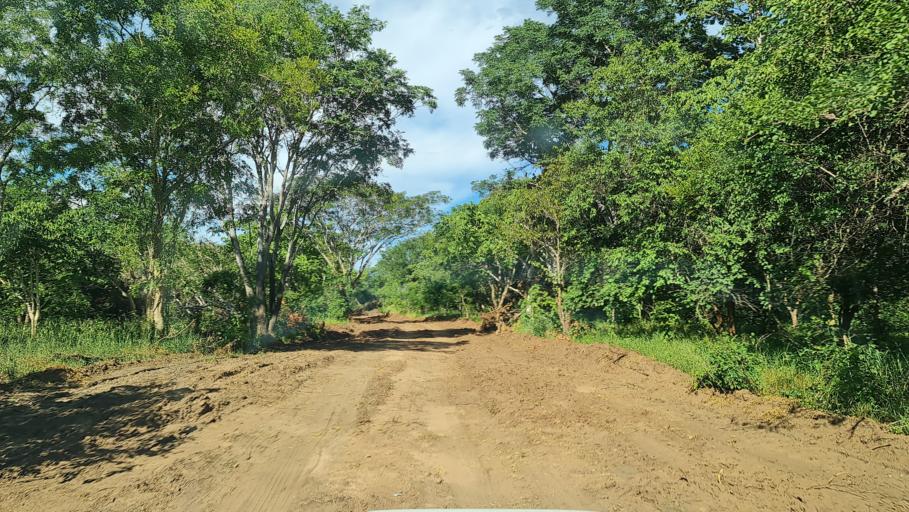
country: MZ
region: Nampula
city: Antonio Enes
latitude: -15.5098
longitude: 40.1353
